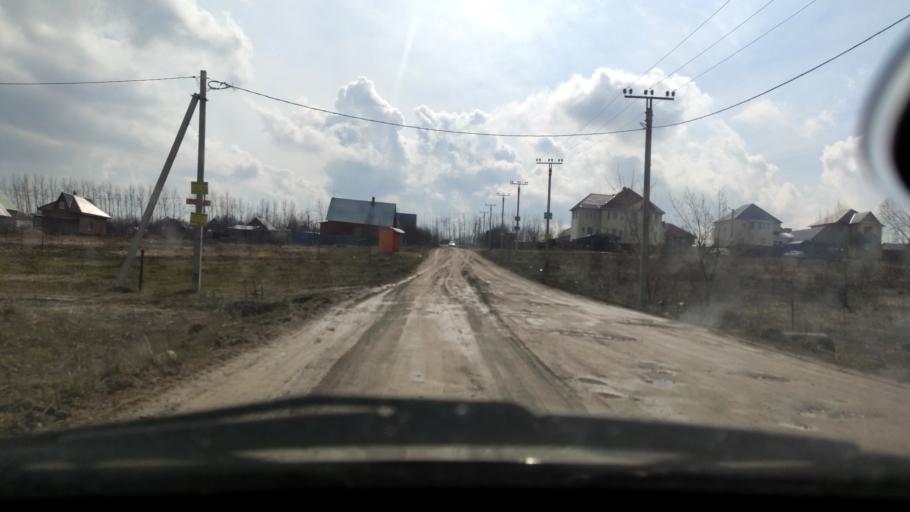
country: RU
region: Bashkortostan
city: Iglino
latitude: 54.7960
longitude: 56.2749
